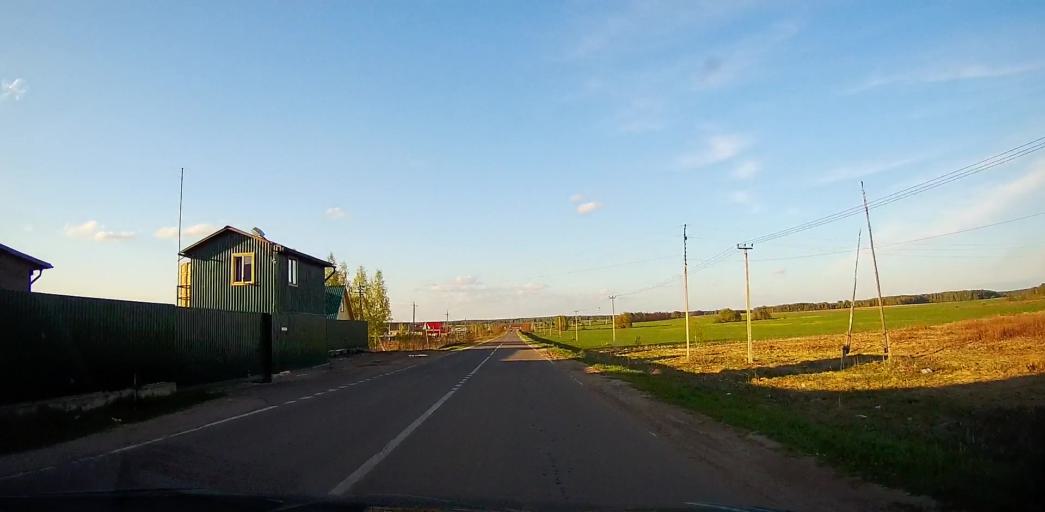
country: RU
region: Moskovskaya
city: Malino
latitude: 55.2775
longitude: 38.1686
